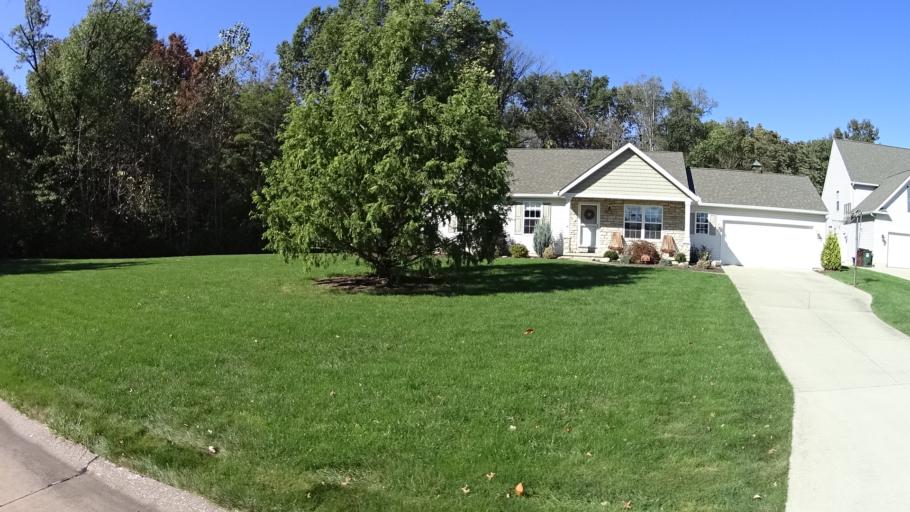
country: US
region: Ohio
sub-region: Lorain County
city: Amherst
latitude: 41.3983
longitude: -82.1994
